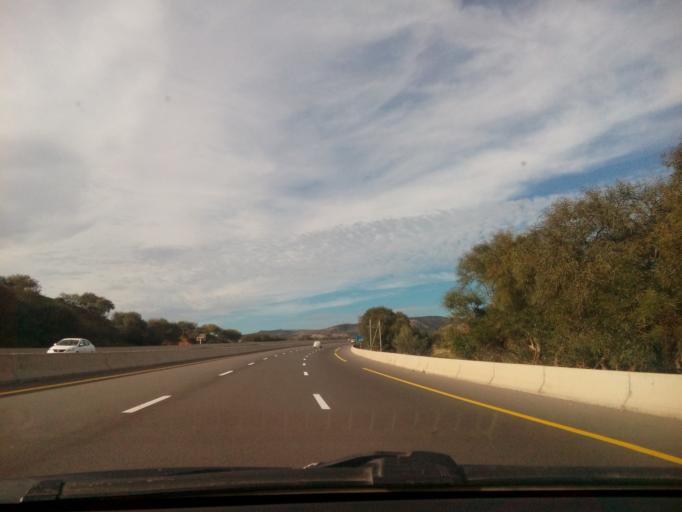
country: DZ
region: Sidi Bel Abbes
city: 'Ain el Berd
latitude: 35.4359
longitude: -0.4300
